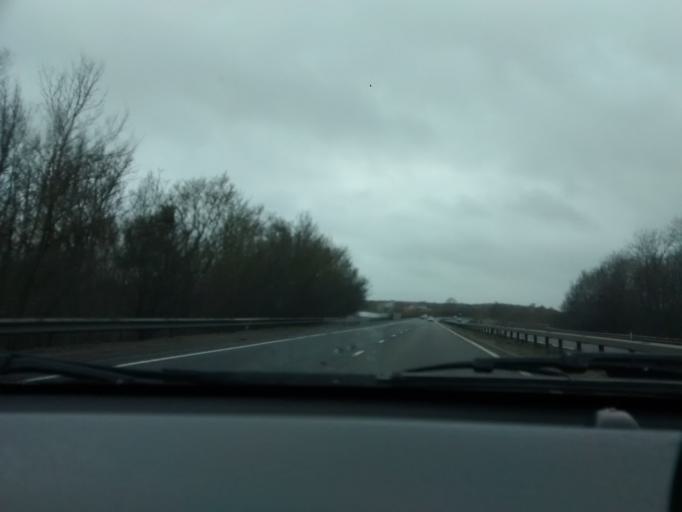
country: GB
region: England
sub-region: Suffolk
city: Stowmarket
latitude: 52.1974
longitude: 0.9967
